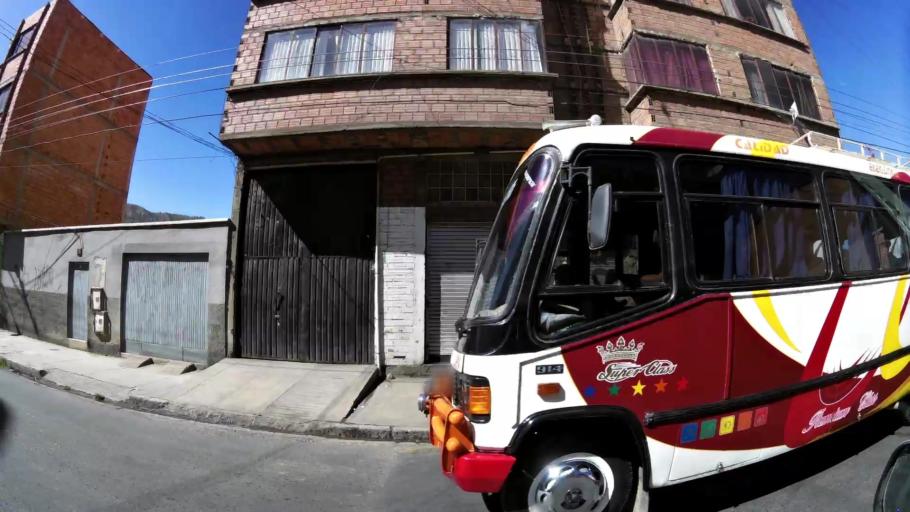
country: BO
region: La Paz
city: La Paz
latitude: -16.4897
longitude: -68.1463
